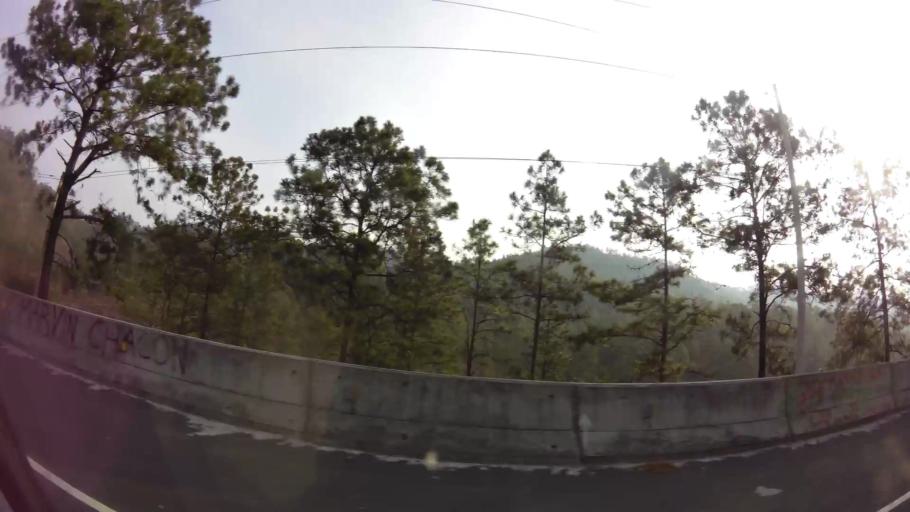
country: HN
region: Francisco Morazan
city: Zambrano
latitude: 14.2894
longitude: -87.4728
